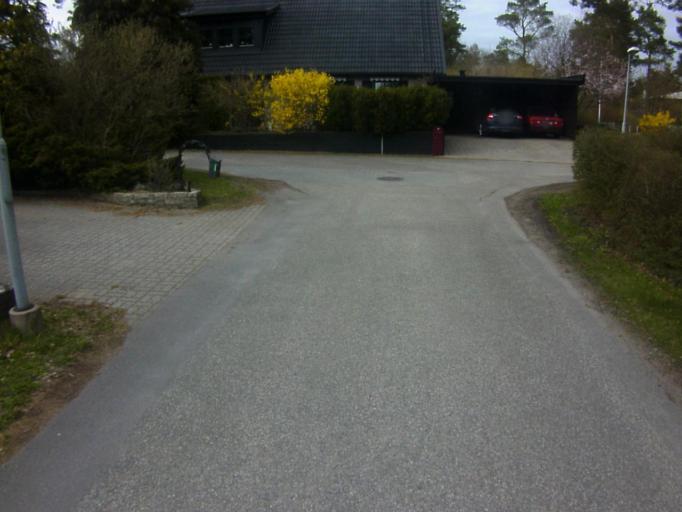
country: SE
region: Skane
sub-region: Kavlinge Kommun
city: Hofterup
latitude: 55.7936
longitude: 12.9711
